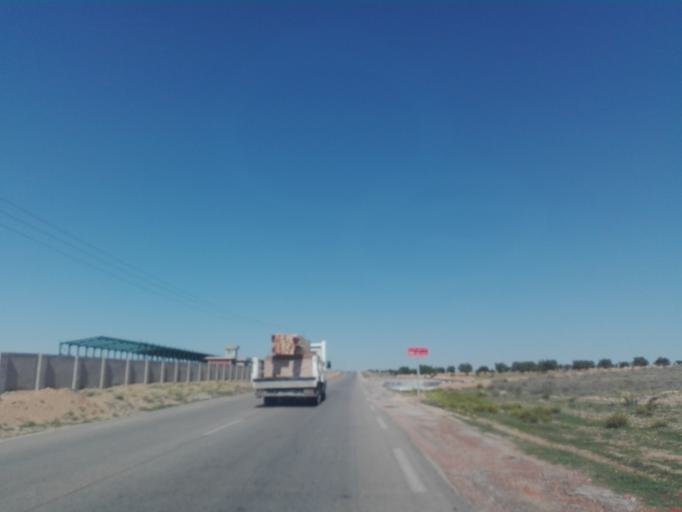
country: TN
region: Safaqis
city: Bi'r `Ali Bin Khalifah
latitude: 34.7345
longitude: 10.4164
